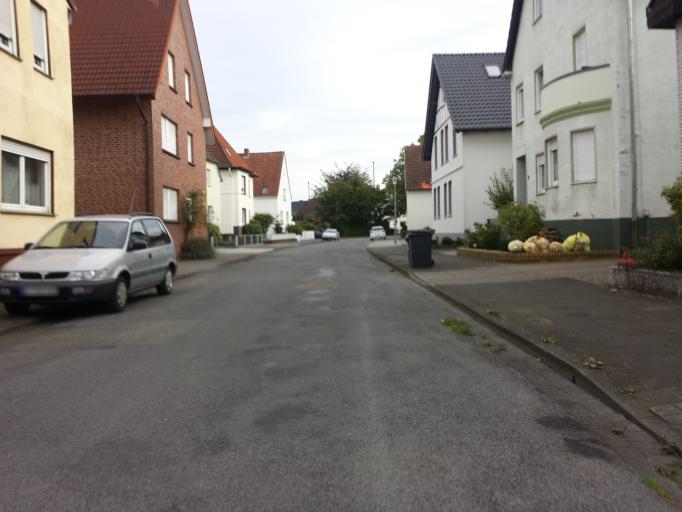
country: DE
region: North Rhine-Westphalia
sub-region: Regierungsbezirk Detmold
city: Guetersloh
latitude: 51.9131
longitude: 8.3640
